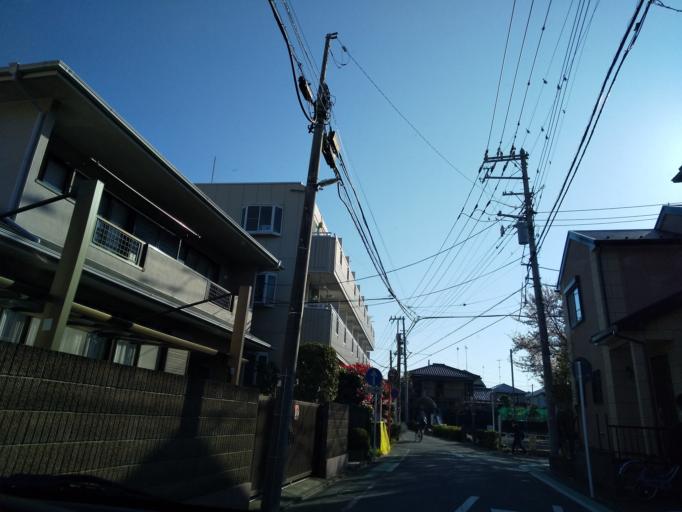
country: JP
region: Kanagawa
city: Zama
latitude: 35.5585
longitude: 139.3819
